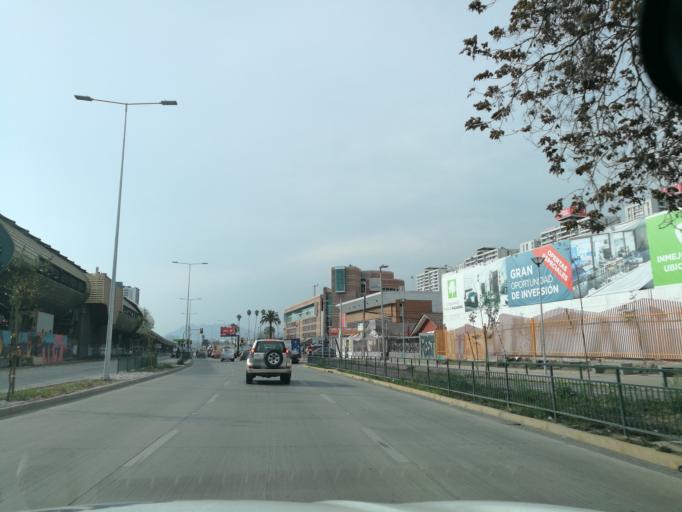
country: CL
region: Santiago Metropolitan
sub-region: Provincia de Santiago
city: Santiago
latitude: -33.4929
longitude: -70.6170
